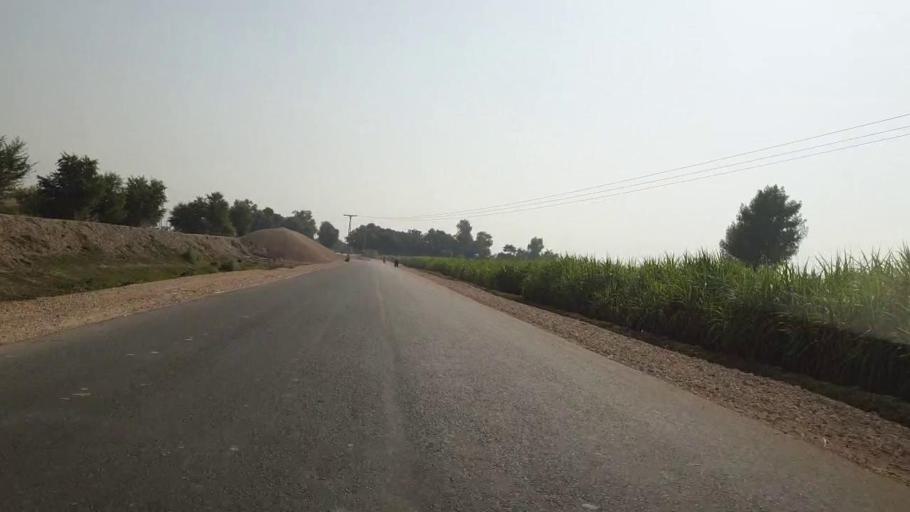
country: PK
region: Sindh
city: Bhan
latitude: 26.6021
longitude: 67.7793
